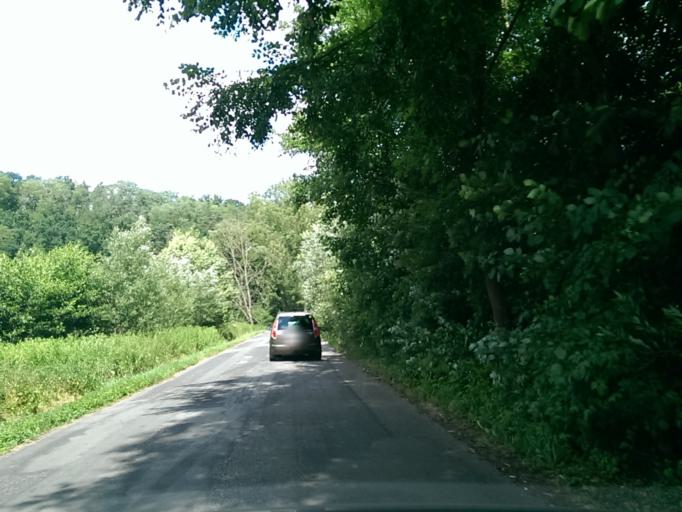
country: CZ
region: Central Bohemia
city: Mseno
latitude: 50.3984
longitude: 14.5580
